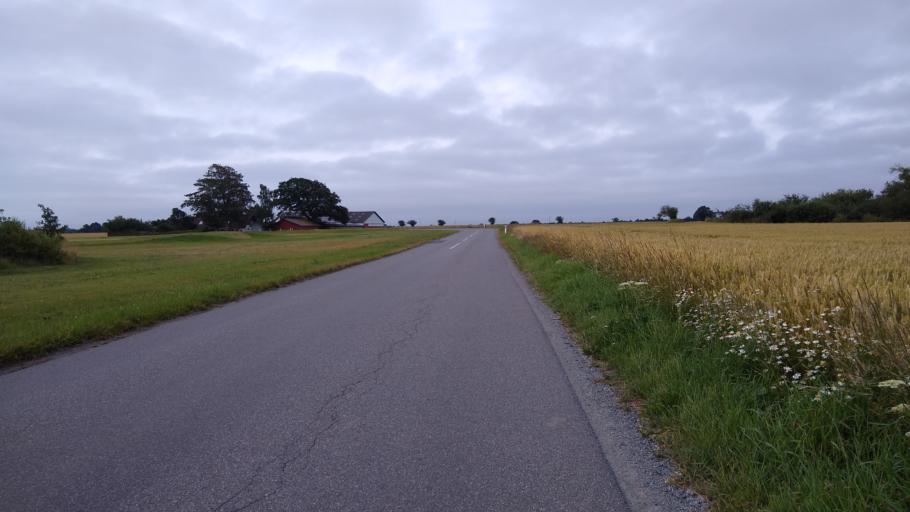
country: DK
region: South Denmark
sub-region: Vejle Kommune
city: Brejning
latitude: 55.6534
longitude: 9.6835
